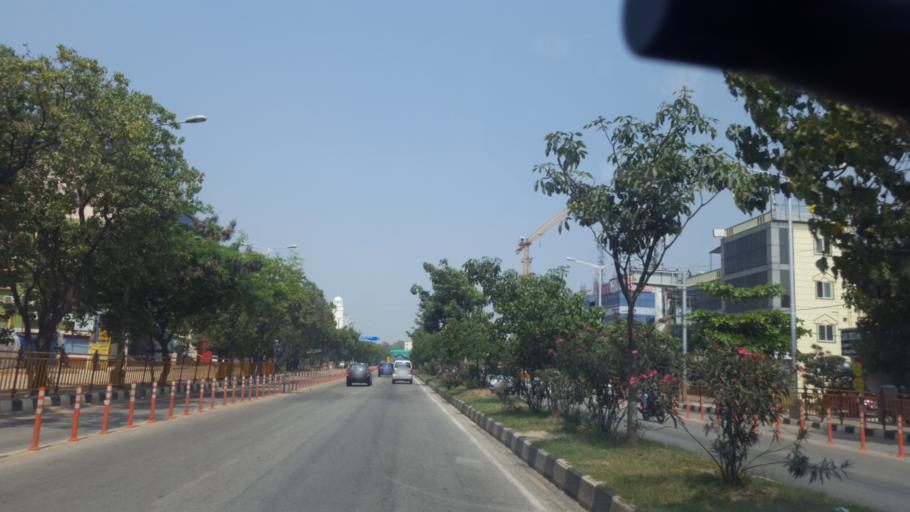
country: IN
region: Karnataka
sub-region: Bangalore Urban
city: Bangalore
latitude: 12.9619
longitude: 77.7016
